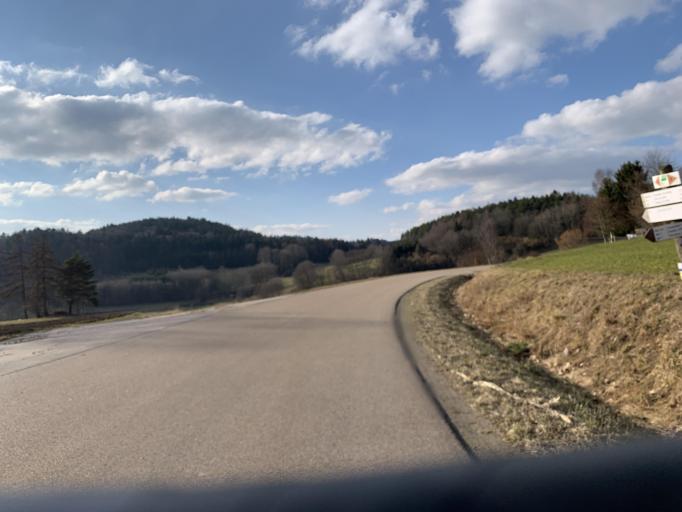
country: DE
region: Bavaria
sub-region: Upper Palatinate
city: Thanstein
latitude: 49.3811
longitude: 12.4591
